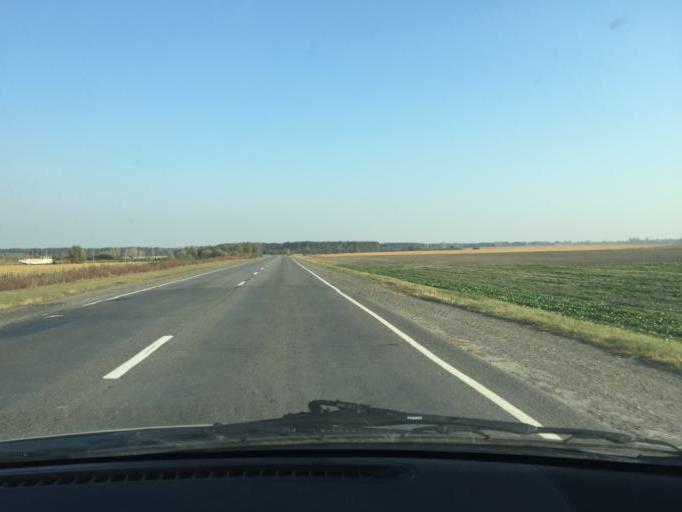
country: BY
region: Brest
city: Davyd-Haradok
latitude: 52.2517
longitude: 27.0615
